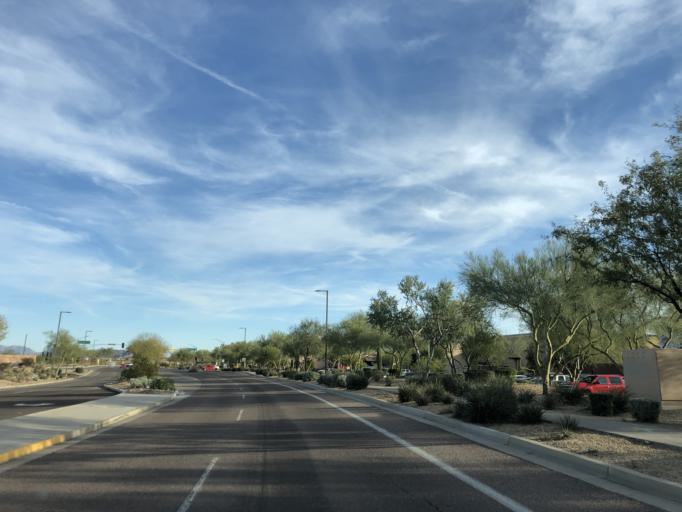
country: US
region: Arizona
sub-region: Maricopa County
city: Anthem
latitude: 33.7161
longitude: -112.1126
